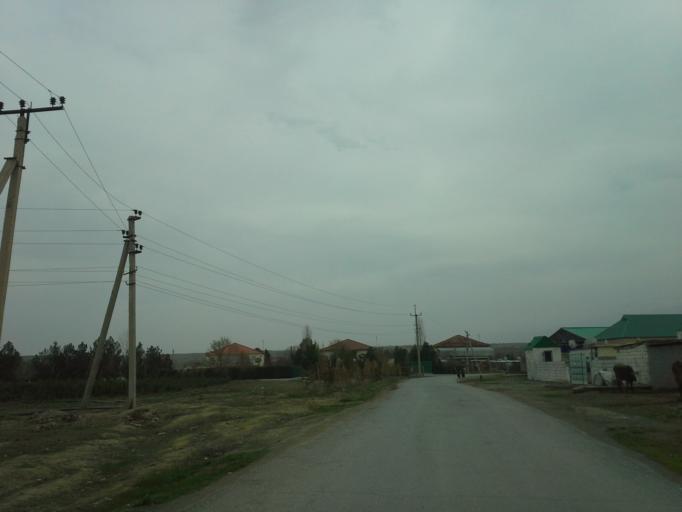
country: TM
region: Ahal
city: Abadan
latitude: 37.9715
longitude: 58.2311
